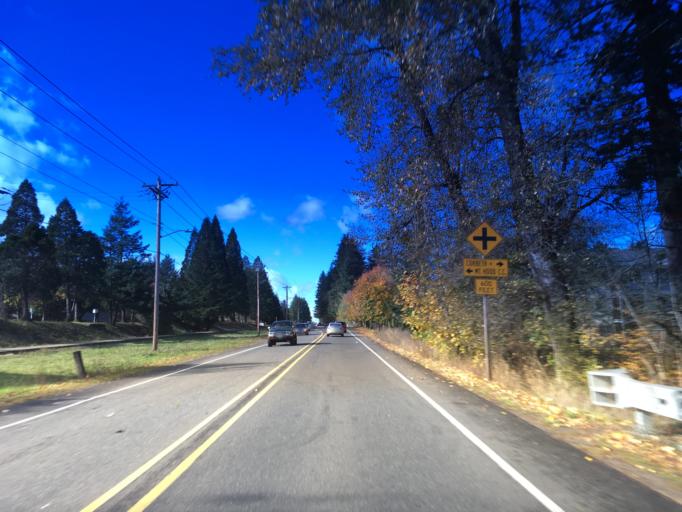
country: US
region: Oregon
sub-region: Multnomah County
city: Troutdale
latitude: 45.5191
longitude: -122.3897
